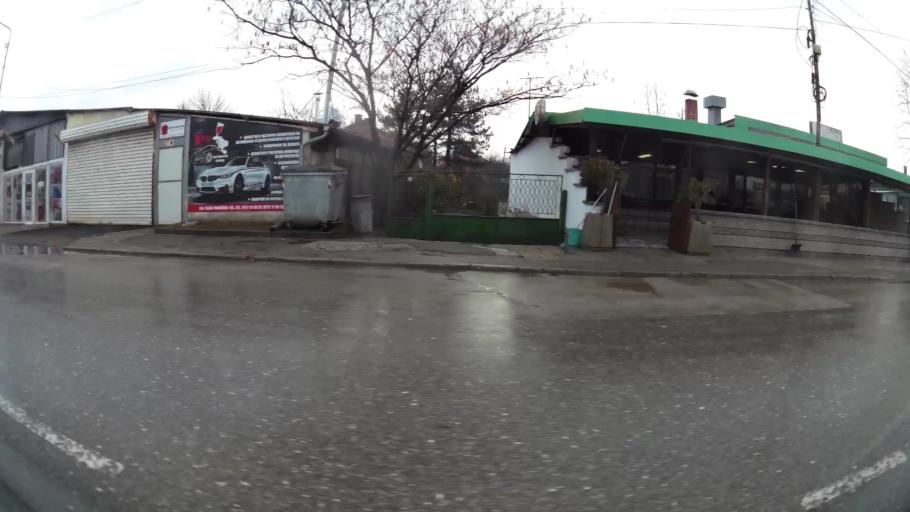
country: BG
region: Sofia-Capital
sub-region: Stolichna Obshtina
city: Sofia
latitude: 42.7344
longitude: 23.3433
